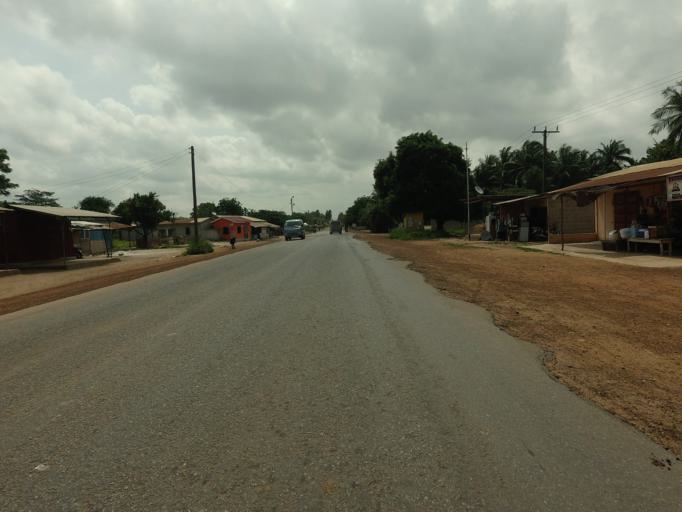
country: TG
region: Maritime
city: Lome
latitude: 6.1202
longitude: 1.1306
